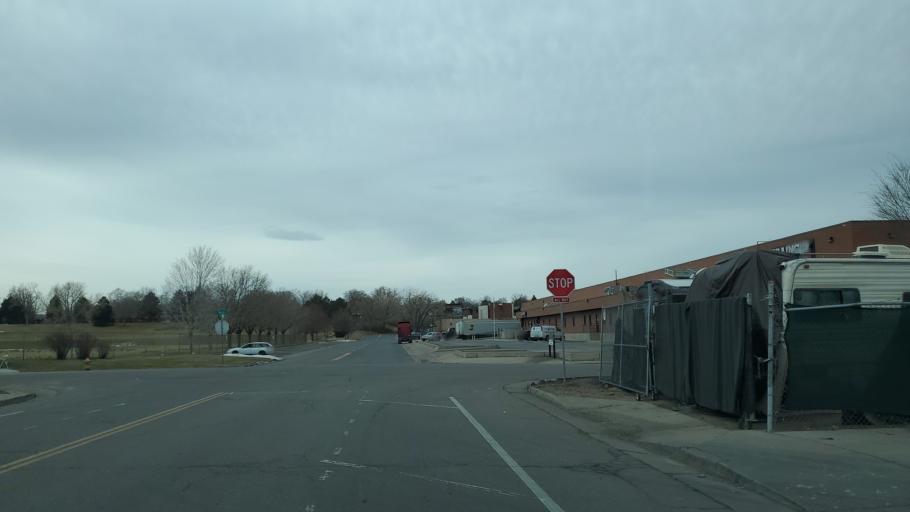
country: US
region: Colorado
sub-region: Denver County
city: Denver
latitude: 39.7149
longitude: -105.0106
